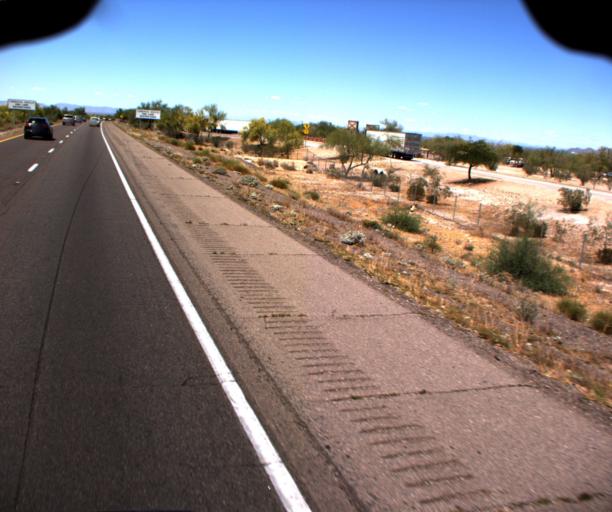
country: US
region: Arizona
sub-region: Pinal County
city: Sacaton
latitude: 33.0264
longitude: -111.7712
